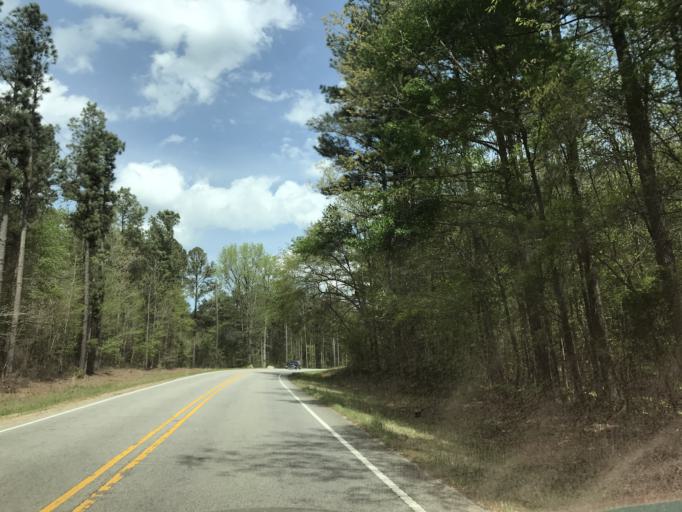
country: US
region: North Carolina
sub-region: Nash County
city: Spring Hope
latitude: 35.9684
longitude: -78.2169
